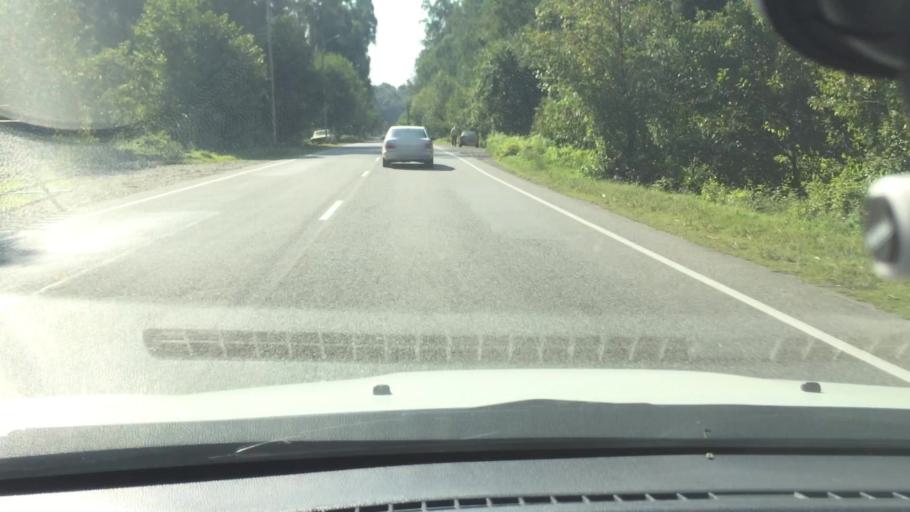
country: GE
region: Guria
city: Urek'i
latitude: 41.9766
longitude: 41.7821
